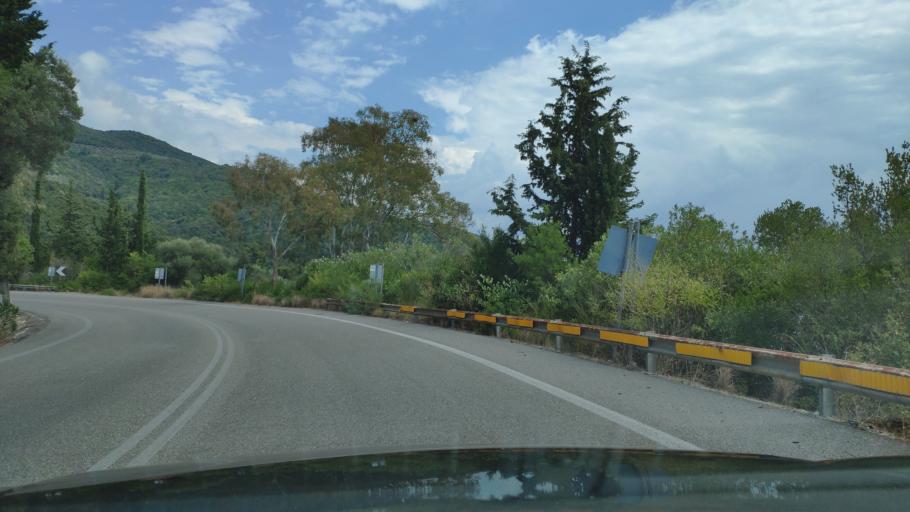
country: GR
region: West Greece
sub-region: Nomos Aitolias kai Akarnanias
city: Menidi
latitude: 39.0246
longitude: 21.1274
